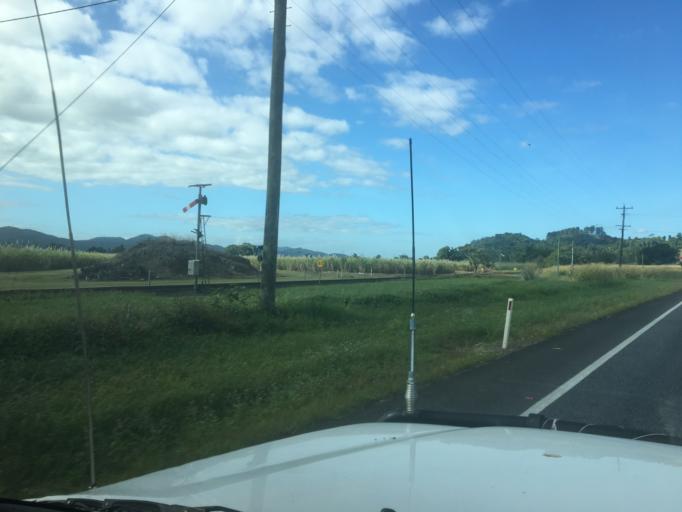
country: AU
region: Queensland
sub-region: Cassowary Coast
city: Innisfail
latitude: -17.2786
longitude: 145.9215
